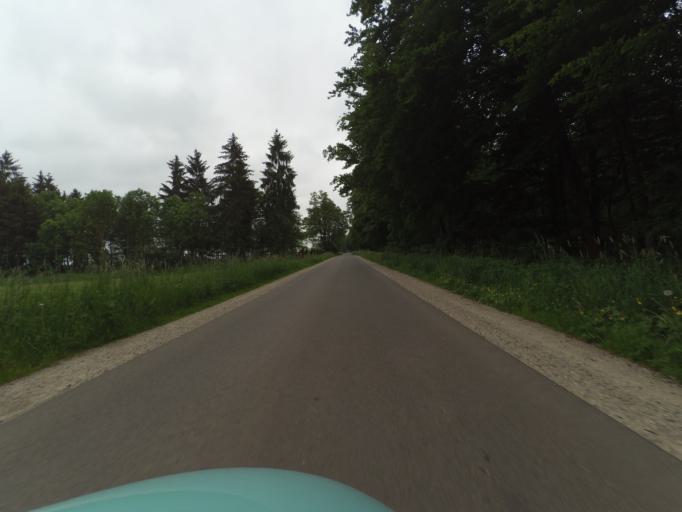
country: DE
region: Lower Saxony
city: Uetze
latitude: 52.4877
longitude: 10.1827
